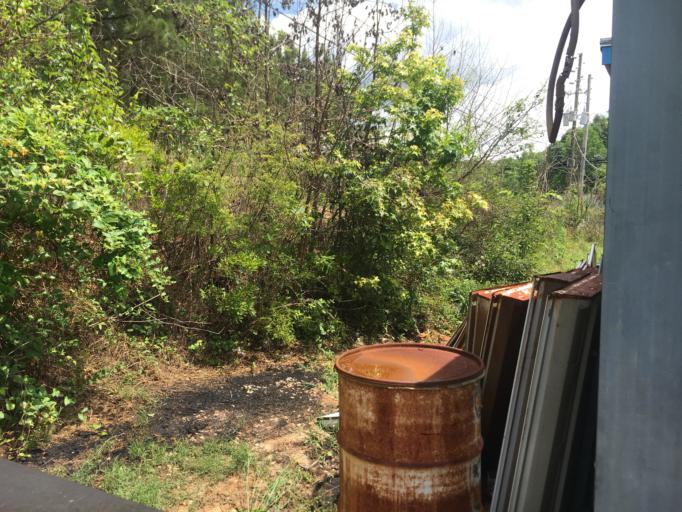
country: US
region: Georgia
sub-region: Troup County
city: La Grange
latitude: 33.0499
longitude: -85.0192
